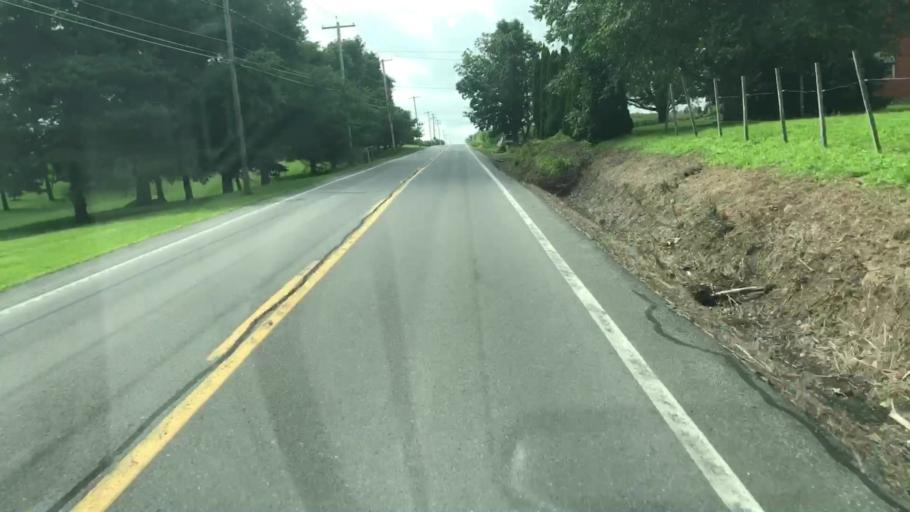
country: US
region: New York
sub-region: Onondaga County
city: Peru
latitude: 43.0456
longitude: -76.3660
